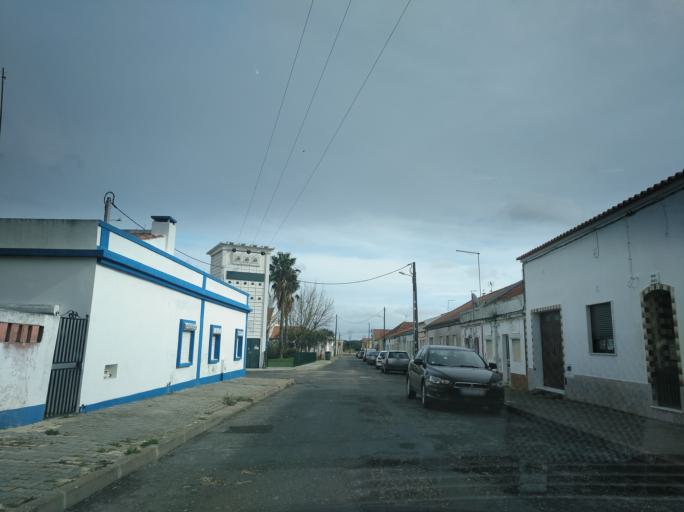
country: PT
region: Setubal
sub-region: Grandola
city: Grandola
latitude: 38.1914
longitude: -8.5552
